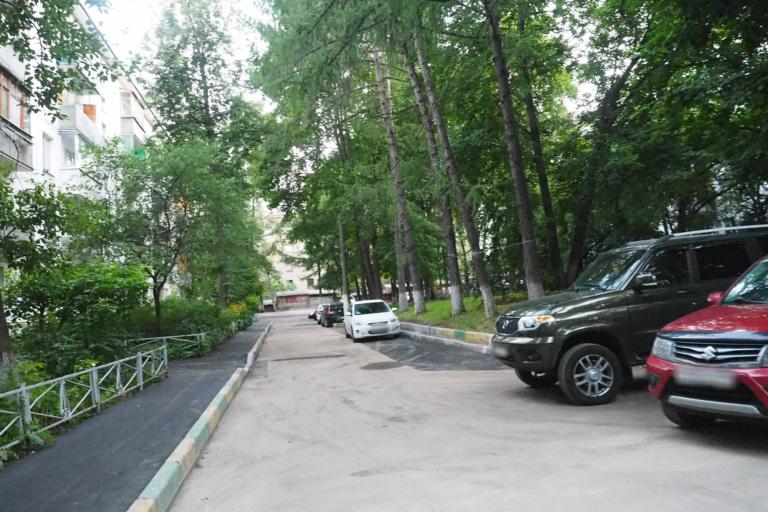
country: RU
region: Moskovskaya
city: Leninskiye Gory
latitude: 55.6816
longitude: 37.5731
